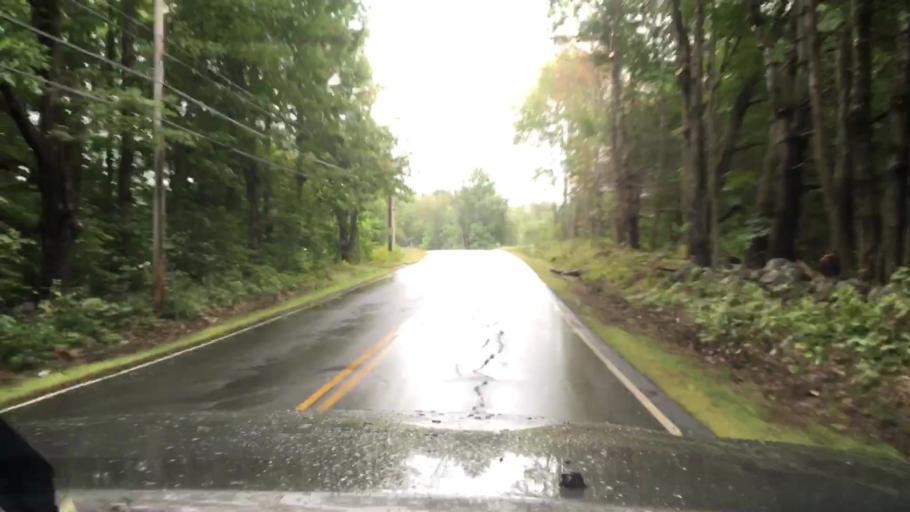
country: US
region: New Hampshire
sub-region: Belknap County
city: Meredith
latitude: 43.6538
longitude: -71.5487
